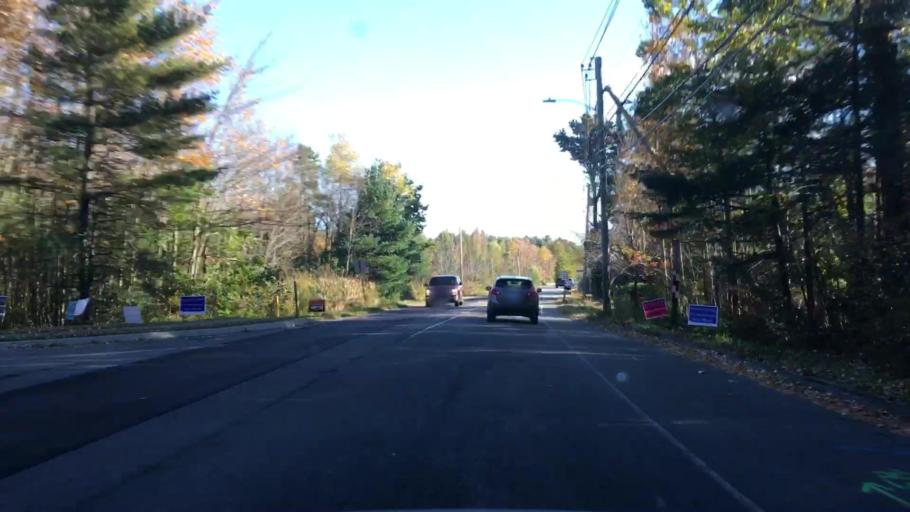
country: US
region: Maine
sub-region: Cumberland County
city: Scarborough
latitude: 43.6053
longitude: -70.3383
